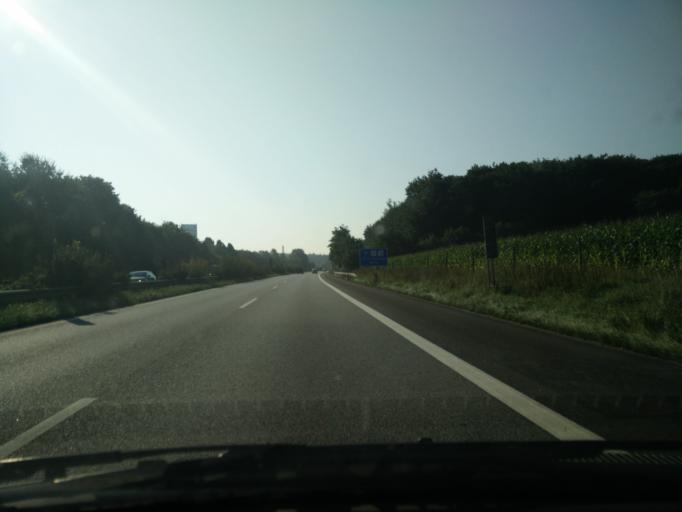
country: DE
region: Schleswig-Holstein
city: Ellerhoop
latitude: 53.7138
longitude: 9.7611
